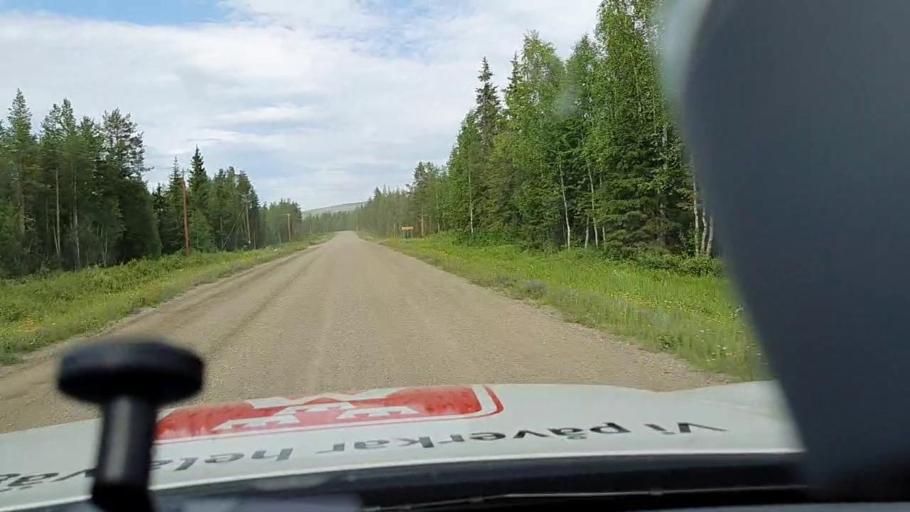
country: SE
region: Norrbotten
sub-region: Alvsbyns Kommun
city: AElvsbyn
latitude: 66.1396
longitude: 21.0089
